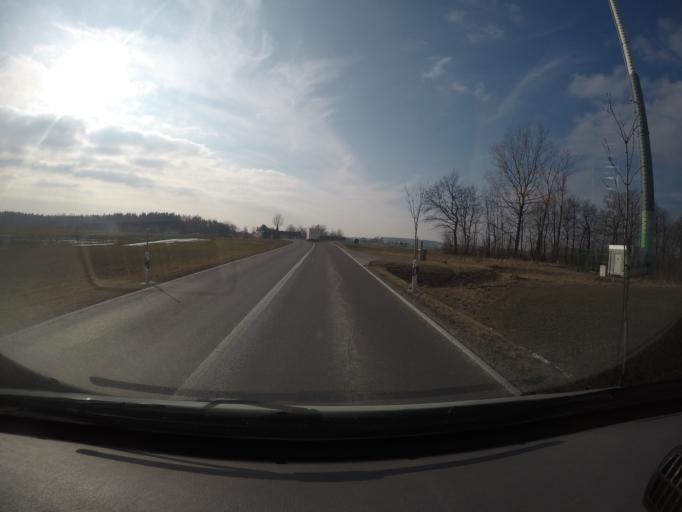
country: DE
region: Saxony
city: Frankenstein
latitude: 50.8775
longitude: 13.2100
